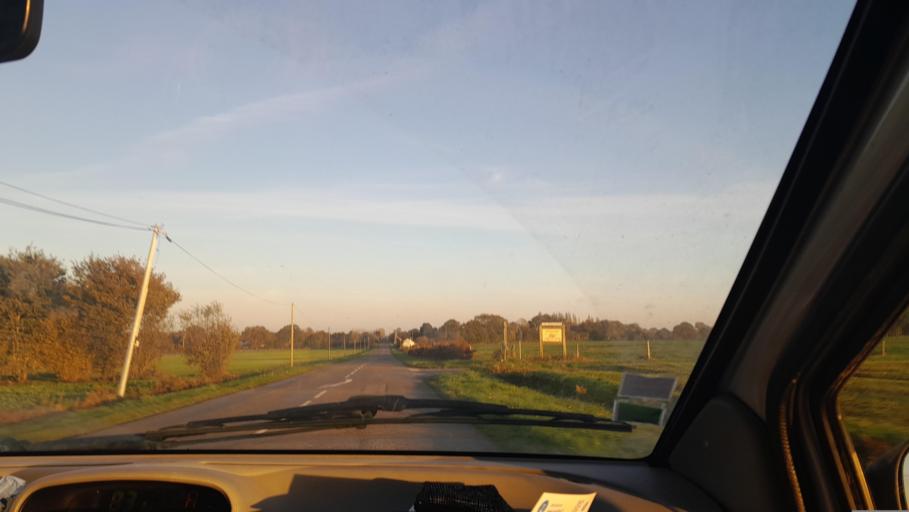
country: FR
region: Brittany
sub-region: Departement d'Ille-et-Vilaine
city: Le Pertre
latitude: 47.9682
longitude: -1.0813
